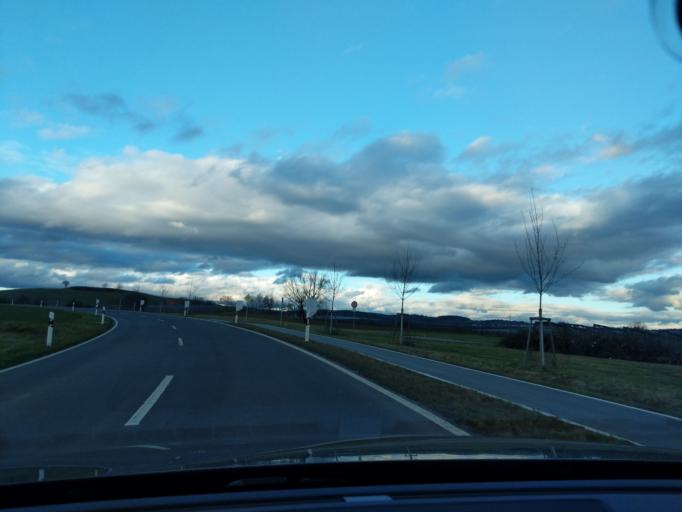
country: DE
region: Baden-Wuerttemberg
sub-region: Tuebingen Region
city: Bermatingen
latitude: 47.7304
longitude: 9.3162
